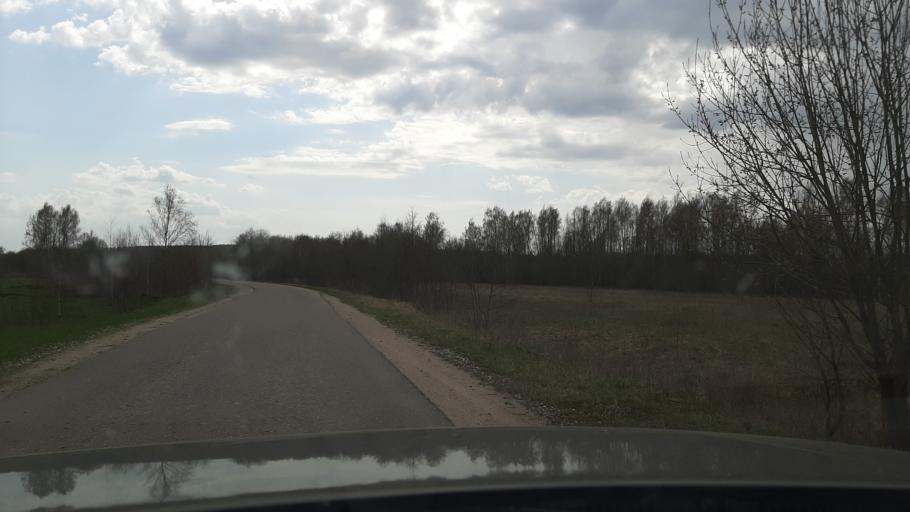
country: RU
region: Ivanovo
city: Furmanov
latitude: 57.3098
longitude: 41.1623
